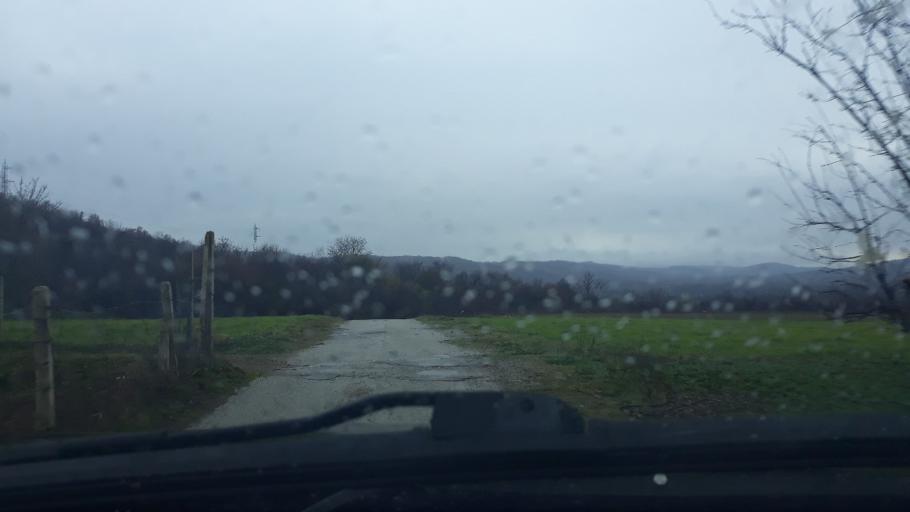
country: MK
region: Bogdanci
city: Bogdanci
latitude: 41.2368
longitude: 22.6500
